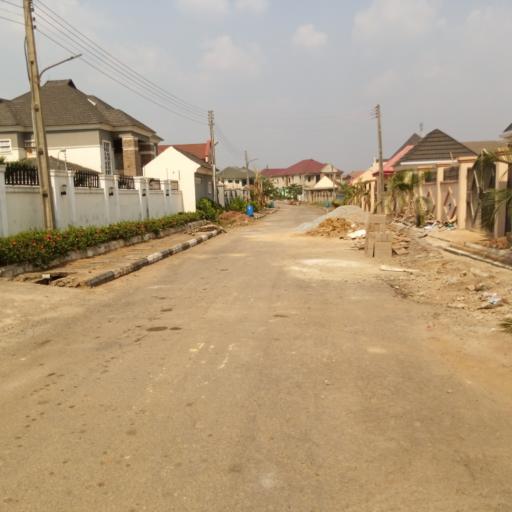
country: NG
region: Oyo
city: Ibadan
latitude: 7.4286
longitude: 3.9093
